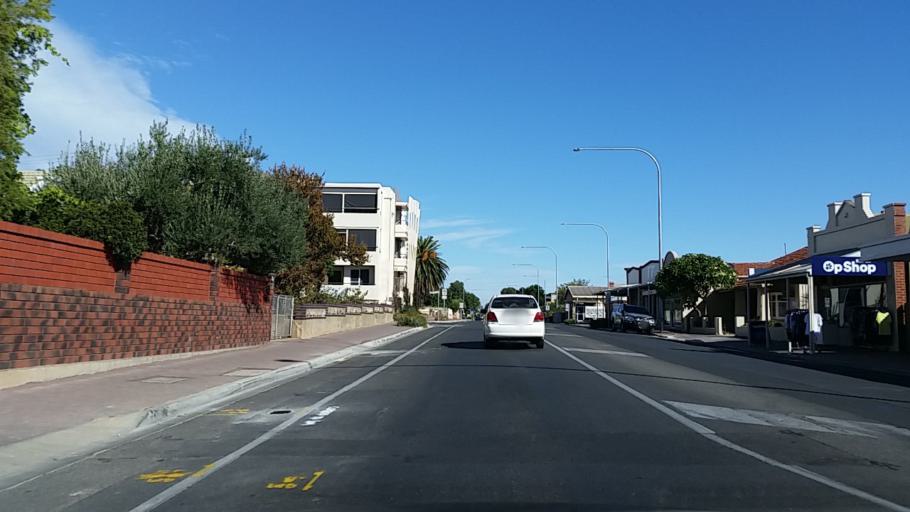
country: AU
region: South Australia
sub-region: Prospect
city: Prospect
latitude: -34.8821
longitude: 138.5937
